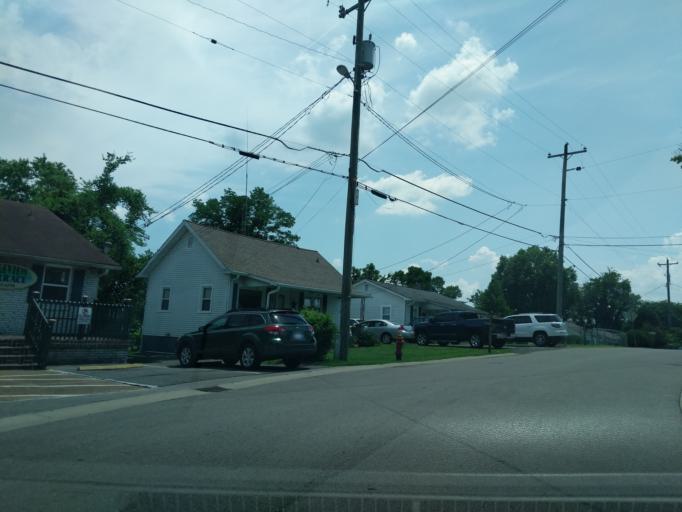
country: US
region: Tennessee
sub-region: Davidson County
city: Lakewood
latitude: 36.2464
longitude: -86.6361
